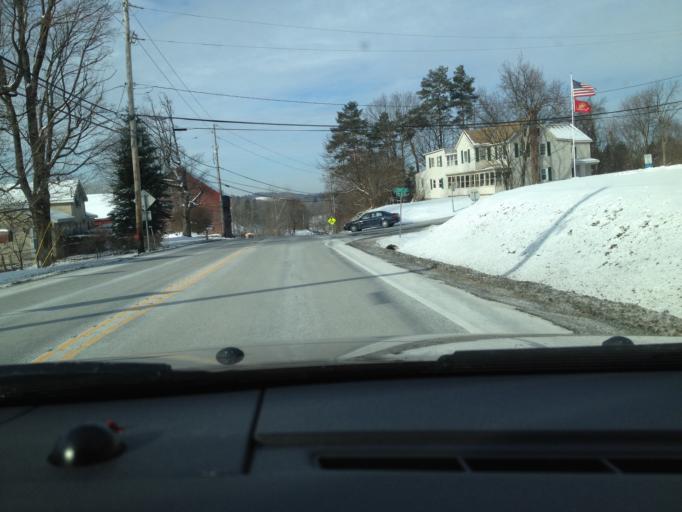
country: US
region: New York
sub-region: Rensselaer County
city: West Sand Lake
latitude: 42.6448
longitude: -73.6371
